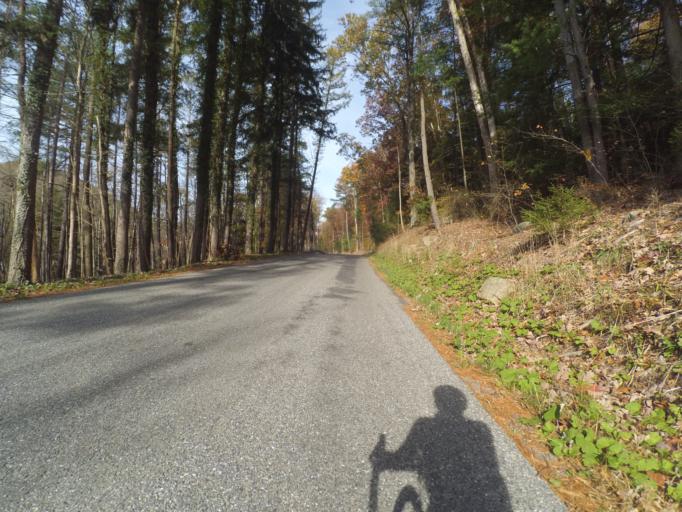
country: US
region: Pennsylvania
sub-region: Centre County
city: Park Forest Village
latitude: 40.9055
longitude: -77.9099
